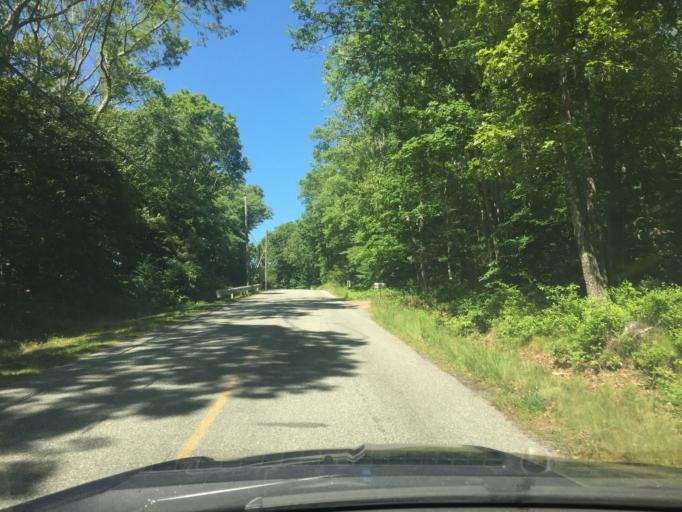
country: US
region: Rhode Island
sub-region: Washington County
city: Hopkinton
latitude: 41.4743
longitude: -71.8140
